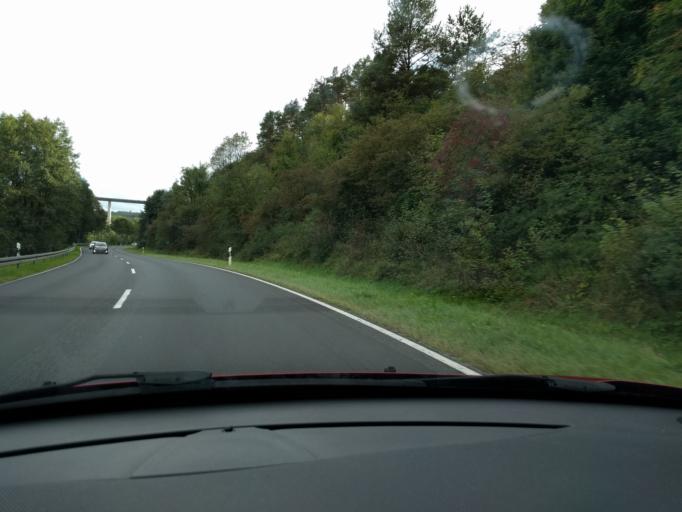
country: DE
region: Thuringia
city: Schwarza
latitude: 50.6056
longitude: 10.5211
